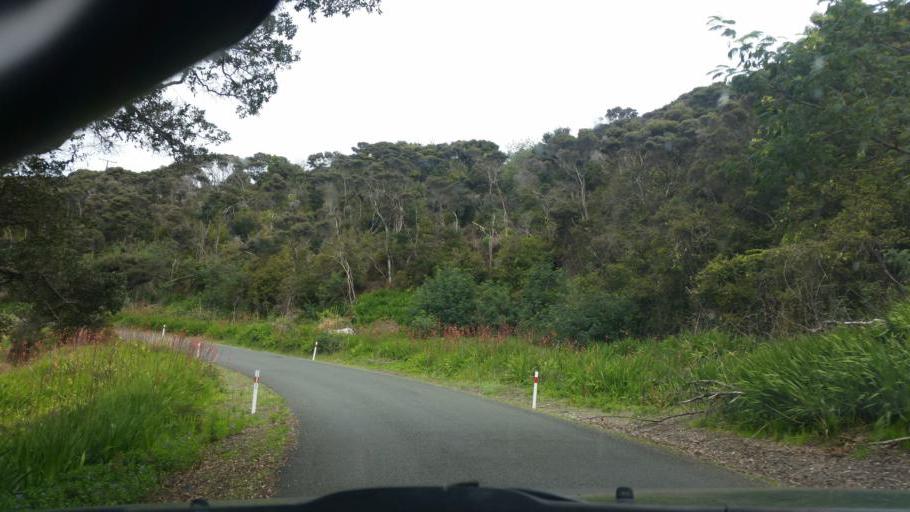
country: NZ
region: Northland
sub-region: Kaipara District
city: Dargaville
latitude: -35.8012
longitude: 173.6272
